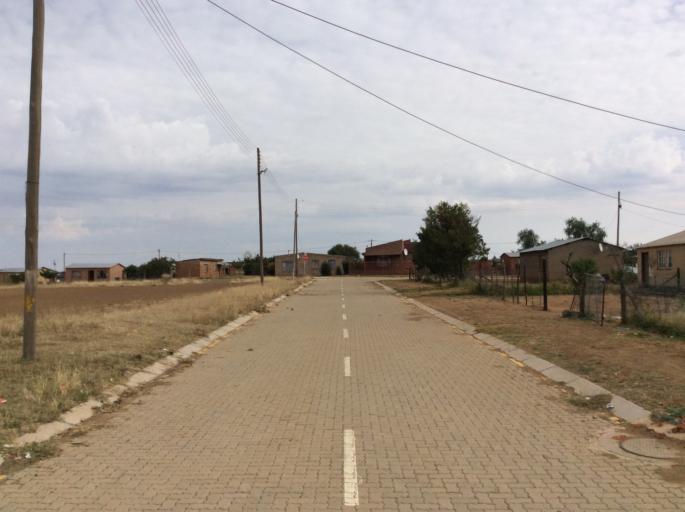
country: LS
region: Mafeteng
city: Mafeteng
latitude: -29.7226
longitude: 27.0091
